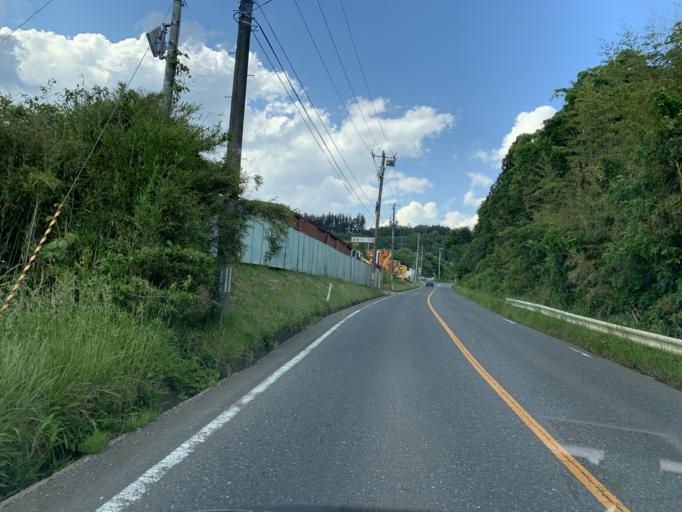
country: JP
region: Miyagi
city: Wakuya
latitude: 38.5607
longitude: 141.1356
